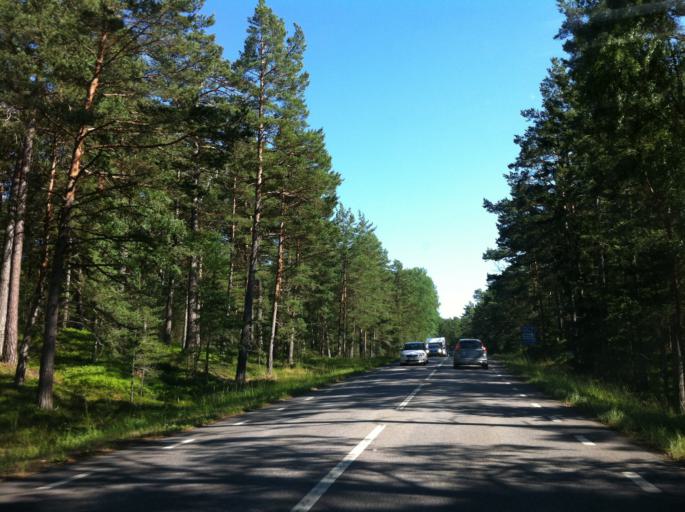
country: SE
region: Kalmar
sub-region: Borgholms Kommun
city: Borgholm
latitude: 57.3014
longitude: 17.0237
